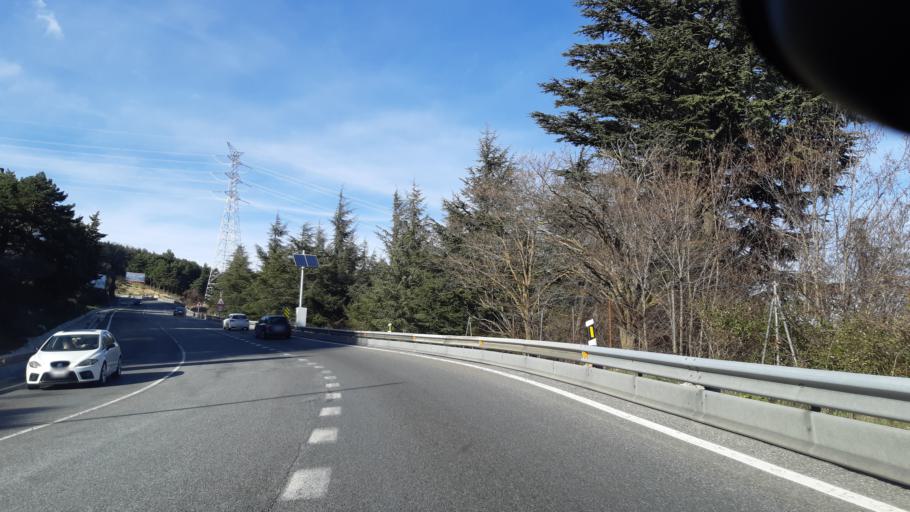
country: ES
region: Madrid
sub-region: Provincia de Madrid
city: Guadarrama
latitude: 40.7070
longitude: -4.1273
